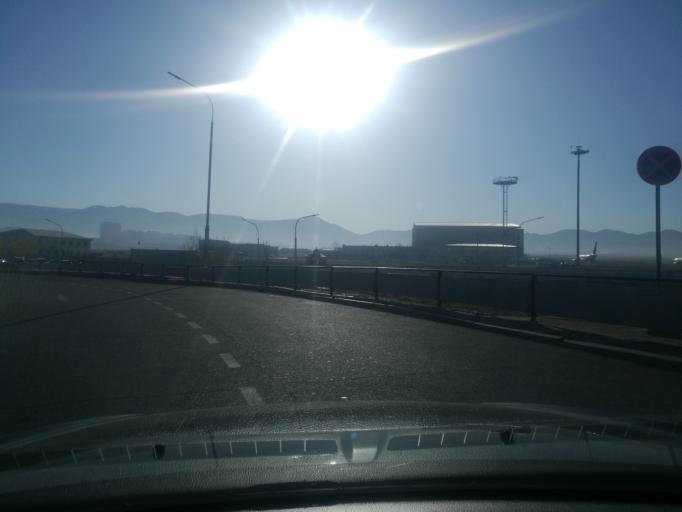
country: MN
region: Ulaanbaatar
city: Ulaanbaatar
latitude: 47.8523
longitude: 106.7639
